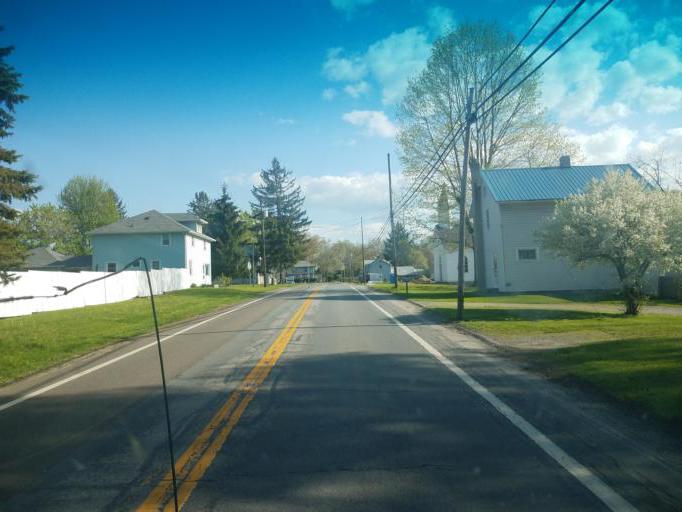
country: US
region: Ohio
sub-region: Wayne County
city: Shreve
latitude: 40.7132
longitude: -81.9451
